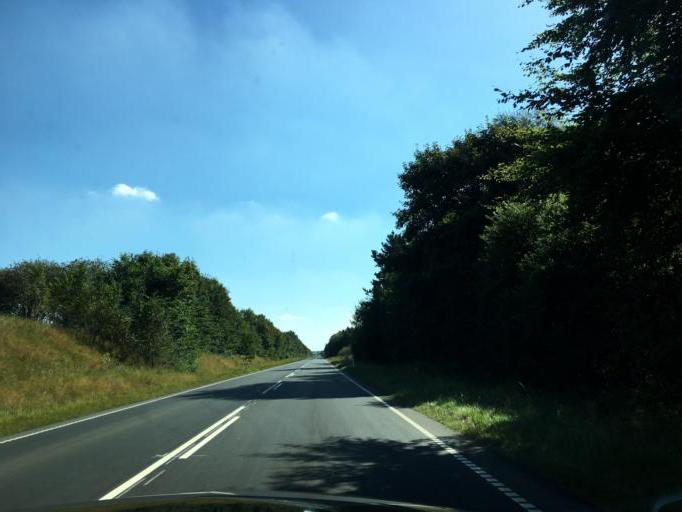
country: DK
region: South Denmark
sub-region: Kolding Kommune
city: Lunderskov
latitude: 55.5017
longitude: 9.2841
